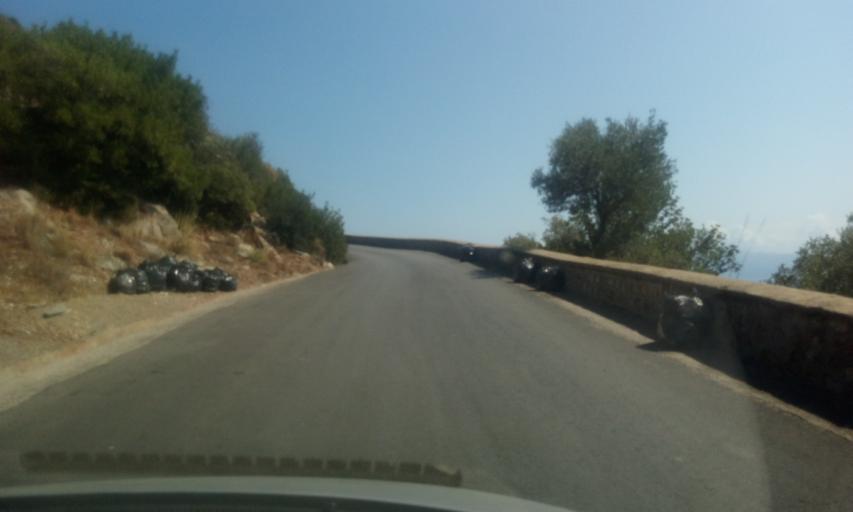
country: DZ
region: Bejaia
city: Bejaia
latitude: 36.7631
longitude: 5.0883
